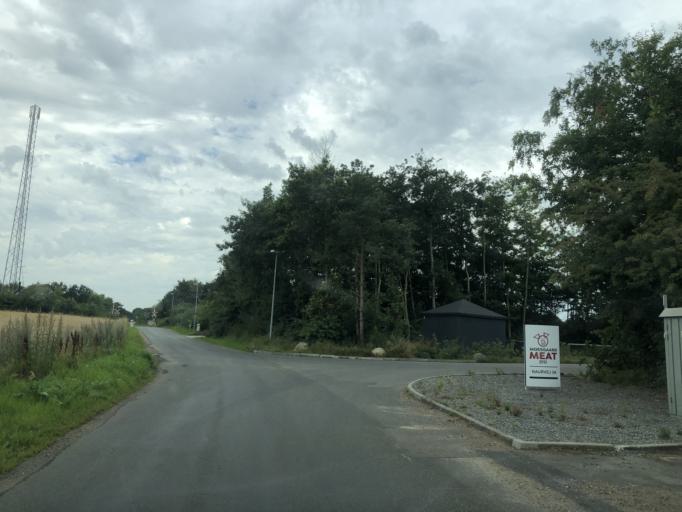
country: DK
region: Central Jutland
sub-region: Holstebro Kommune
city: Holstebro
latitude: 56.3760
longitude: 8.5202
